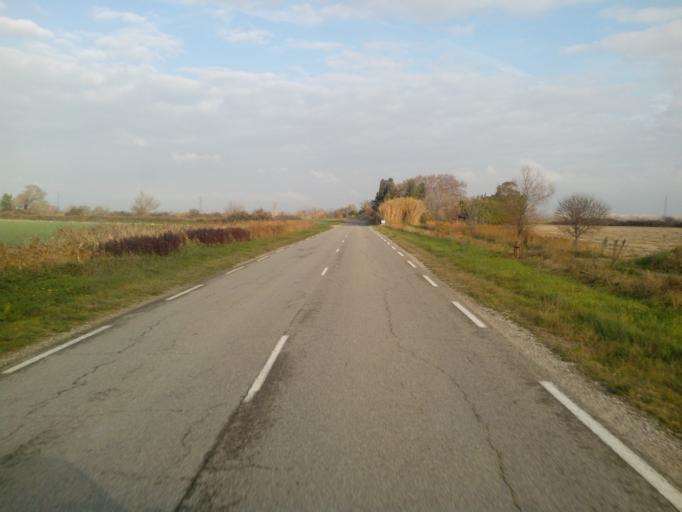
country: FR
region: Provence-Alpes-Cote d'Azur
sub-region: Departement des Bouches-du-Rhone
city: Arles
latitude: 43.5751
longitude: 4.6320
